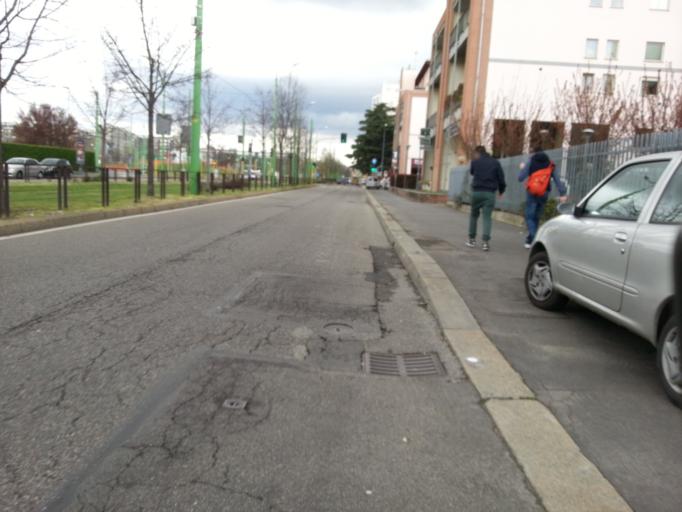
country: IT
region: Lombardy
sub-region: Citta metropolitana di Milano
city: Bresso
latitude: 45.5234
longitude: 9.1925
